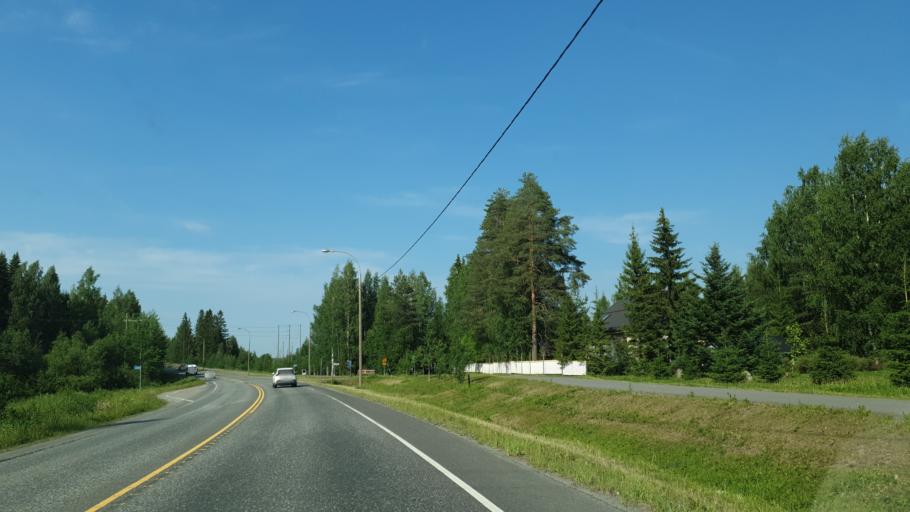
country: FI
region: Northern Savo
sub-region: Kuopio
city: Siilinjaervi
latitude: 63.1166
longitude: 27.7678
